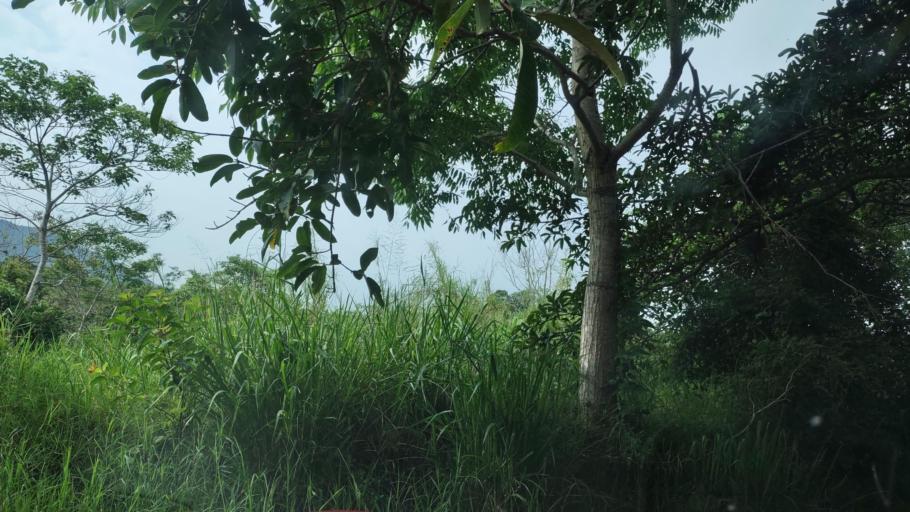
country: MX
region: Veracruz
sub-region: Coatepec
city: Bella Esperanza
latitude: 19.4444
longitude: -96.8261
